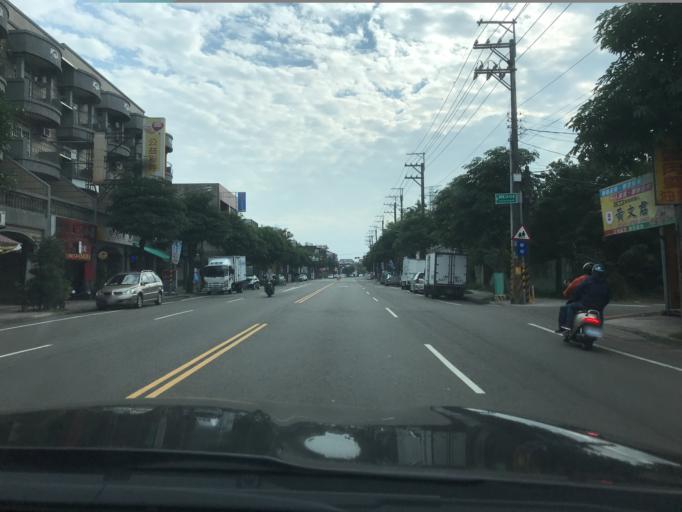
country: TW
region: Taiwan
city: Daxi
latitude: 24.9104
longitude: 121.2796
